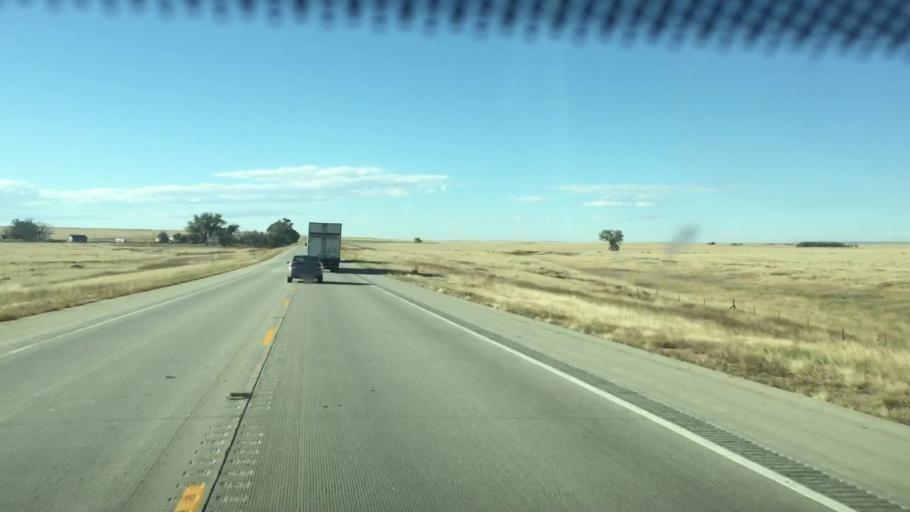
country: US
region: Colorado
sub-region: Lincoln County
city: Hugo
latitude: 38.9332
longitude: -103.2010
